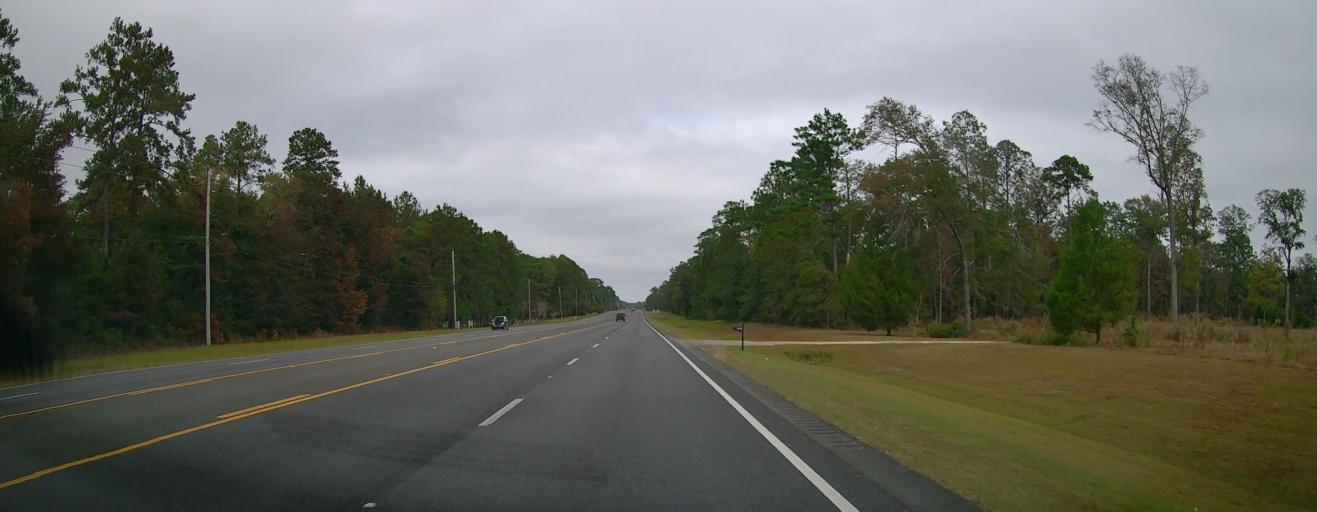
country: US
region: Georgia
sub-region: Thomas County
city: Thomasville
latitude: 30.9046
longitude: -83.9256
